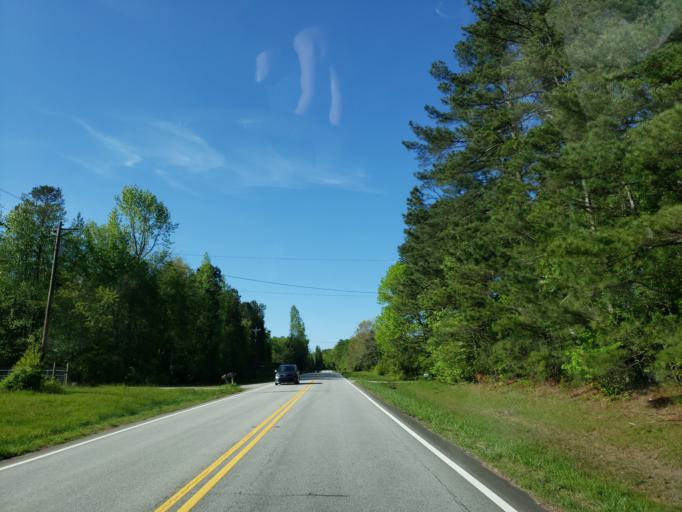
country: US
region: Georgia
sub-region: Haralson County
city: Tallapoosa
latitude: 33.8893
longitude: -85.3117
